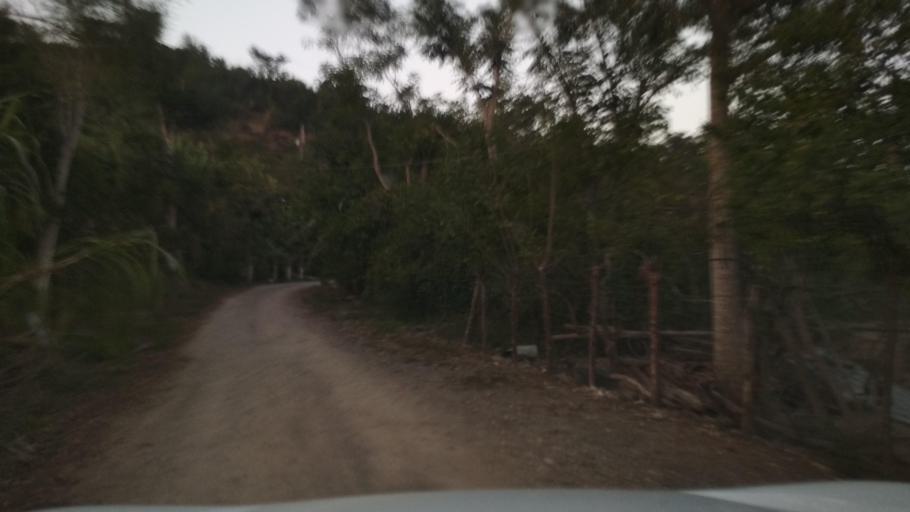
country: MX
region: Veracruz
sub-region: Poza Rica de Hidalgo
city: Arroyo del Maiz Uno
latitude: 20.4747
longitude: -97.3929
